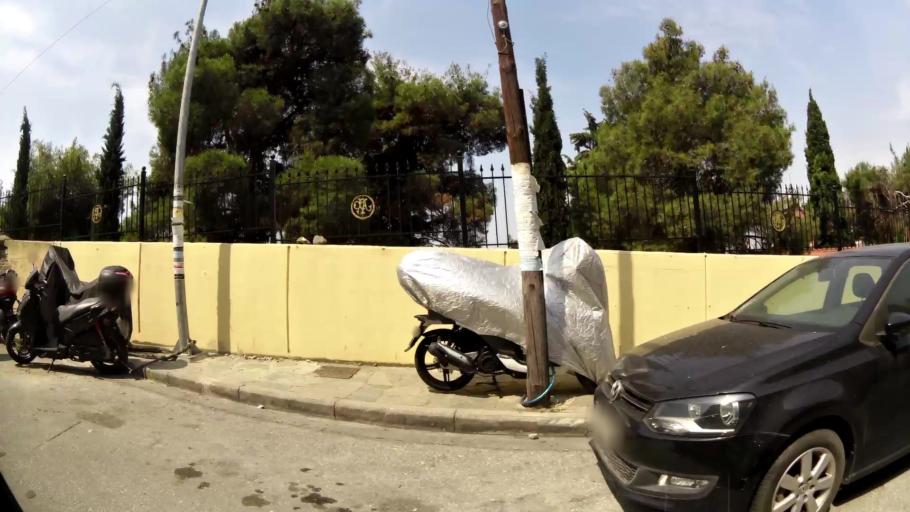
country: GR
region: Central Macedonia
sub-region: Nomos Thessalonikis
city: Agios Pavlos
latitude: 40.6385
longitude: 22.9616
